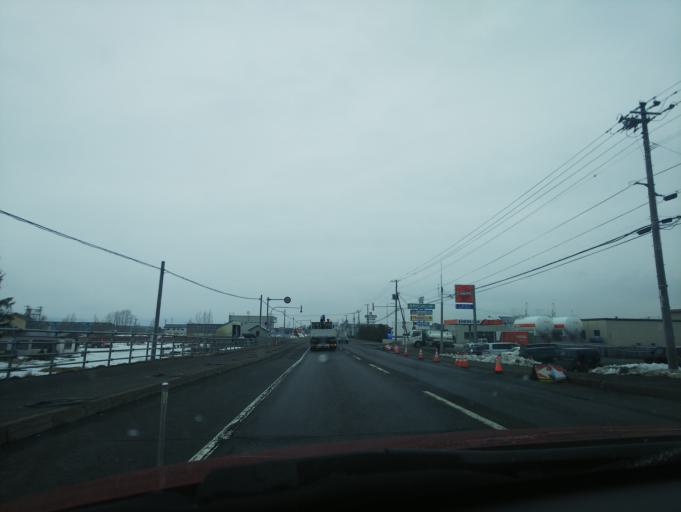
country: JP
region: Hokkaido
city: Nayoro
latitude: 44.1562
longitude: 142.3984
